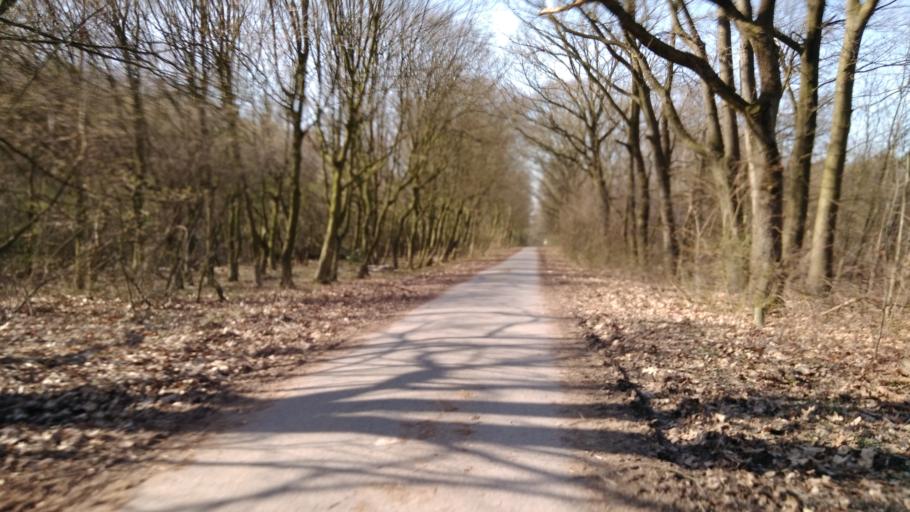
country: DE
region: North Rhine-Westphalia
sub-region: Regierungsbezirk Munster
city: Bottrop
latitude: 51.5576
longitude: 6.8800
